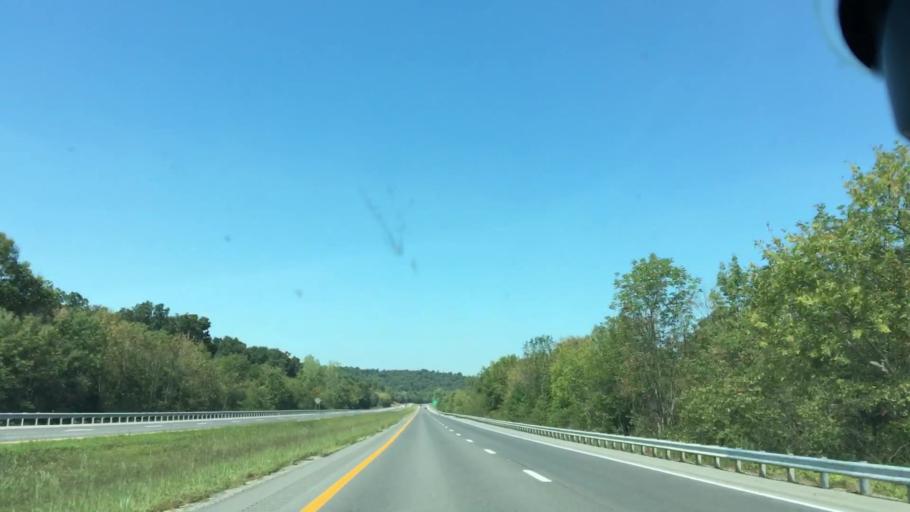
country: US
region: Kentucky
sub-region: Webster County
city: Sebree
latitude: 37.5842
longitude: -87.4861
